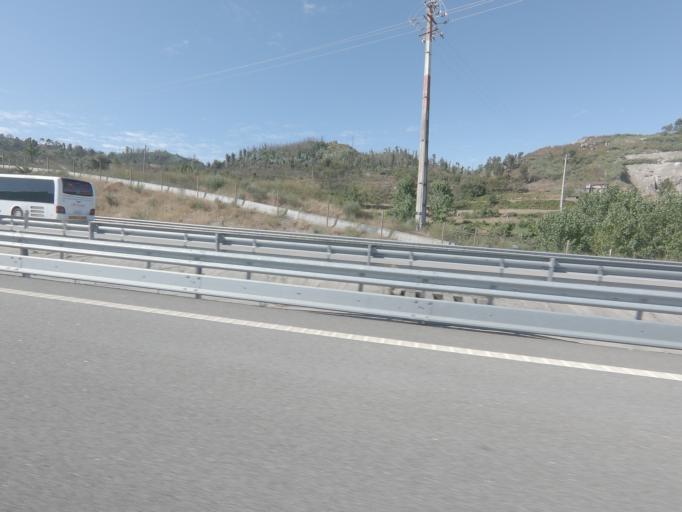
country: PT
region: Porto
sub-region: Amarante
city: Amarante
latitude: 41.2614
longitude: -8.0071
